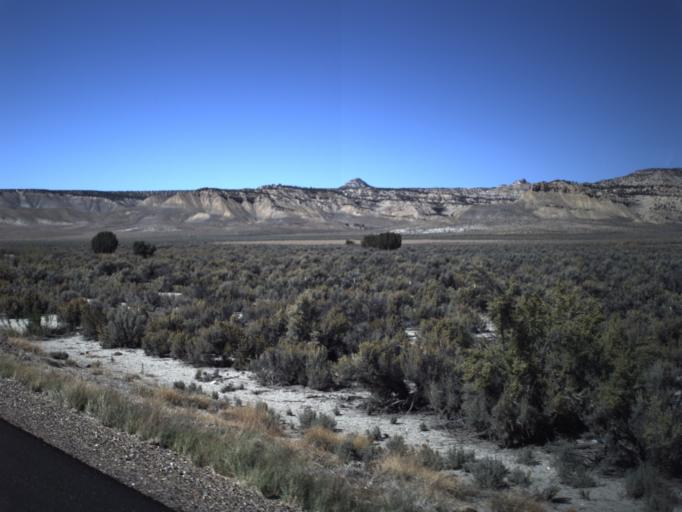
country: US
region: Utah
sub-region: Garfield County
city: Panguitch
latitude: 37.5980
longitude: -111.9504
